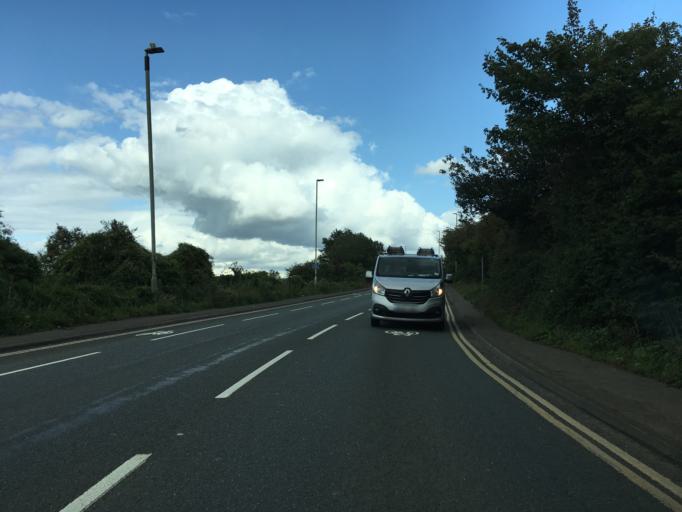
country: GB
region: England
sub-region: Gloucestershire
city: Gloucester
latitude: 51.8467
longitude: -2.2624
